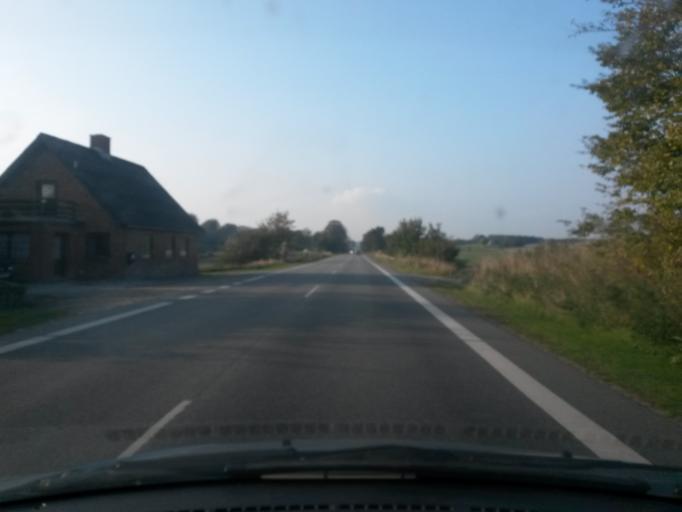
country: DK
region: Central Jutland
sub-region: Syddjurs Kommune
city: Hornslet
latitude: 56.3591
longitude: 10.3370
